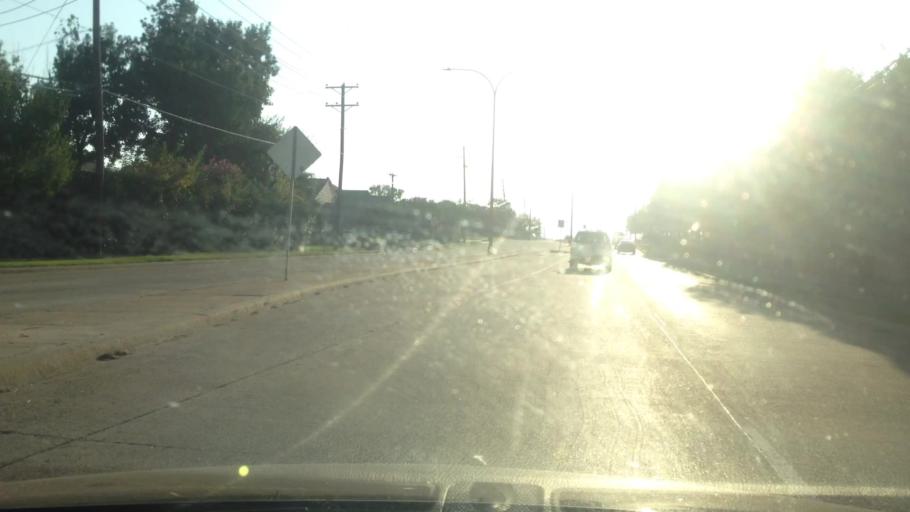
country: US
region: Texas
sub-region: Tarrant County
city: Dalworthington Gardens
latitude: 32.6826
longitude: -97.1832
